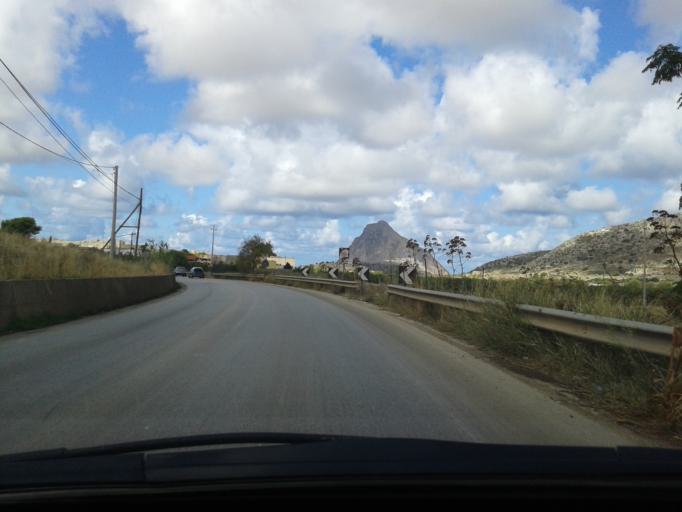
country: IT
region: Sicily
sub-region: Trapani
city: Castelluzzo
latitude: 38.0790
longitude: 12.7205
